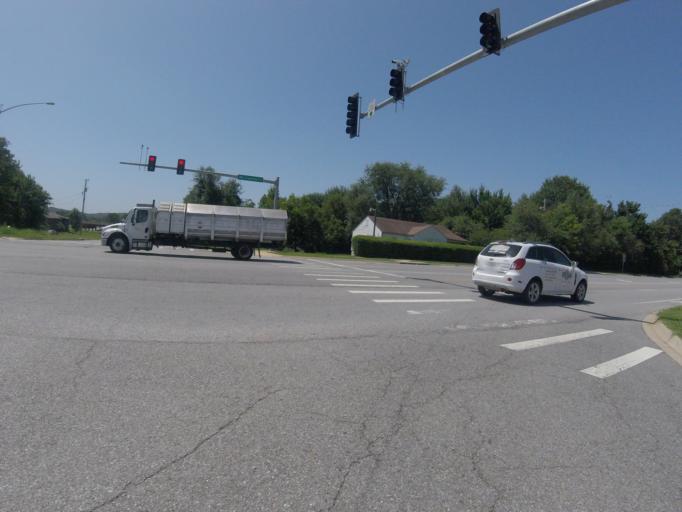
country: US
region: Arkansas
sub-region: Washington County
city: Fayetteville
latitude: 36.0929
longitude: -94.1939
